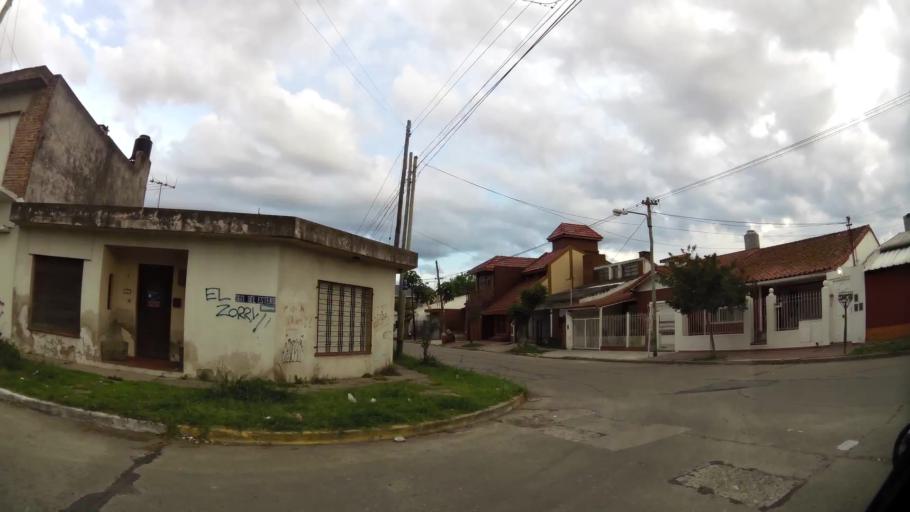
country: AR
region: Buenos Aires
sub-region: Partido de Quilmes
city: Quilmes
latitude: -34.7477
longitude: -58.2301
